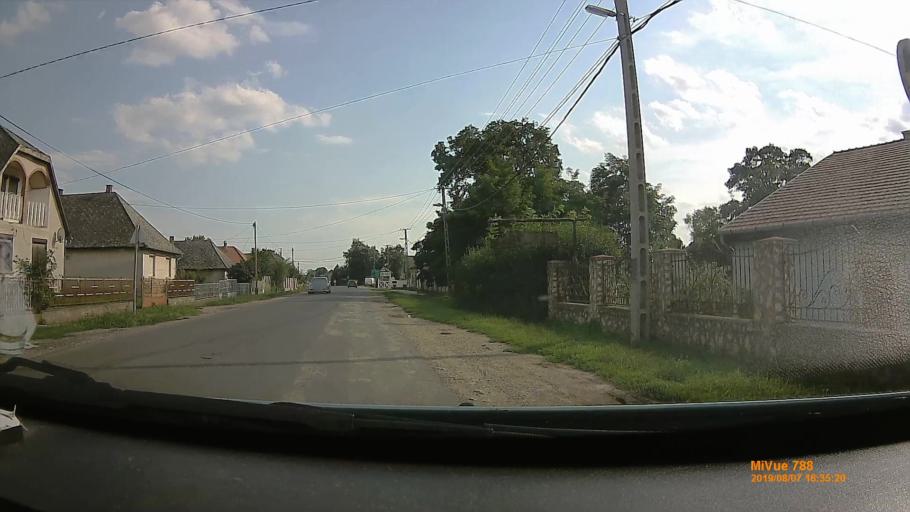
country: HU
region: Borsod-Abauj-Zemplen
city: Gonc
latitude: 48.4140
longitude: 21.2305
